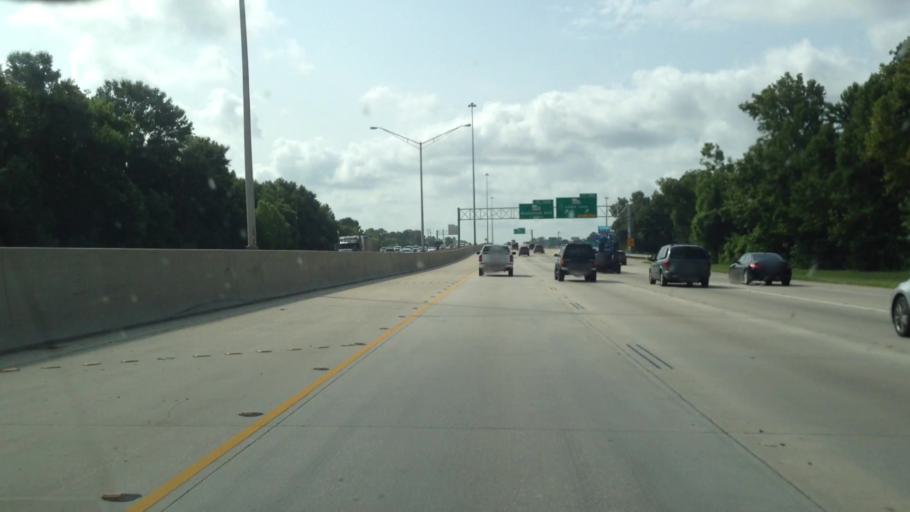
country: US
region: Louisiana
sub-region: East Baton Rouge Parish
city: Westminster
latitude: 30.4119
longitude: -91.1070
